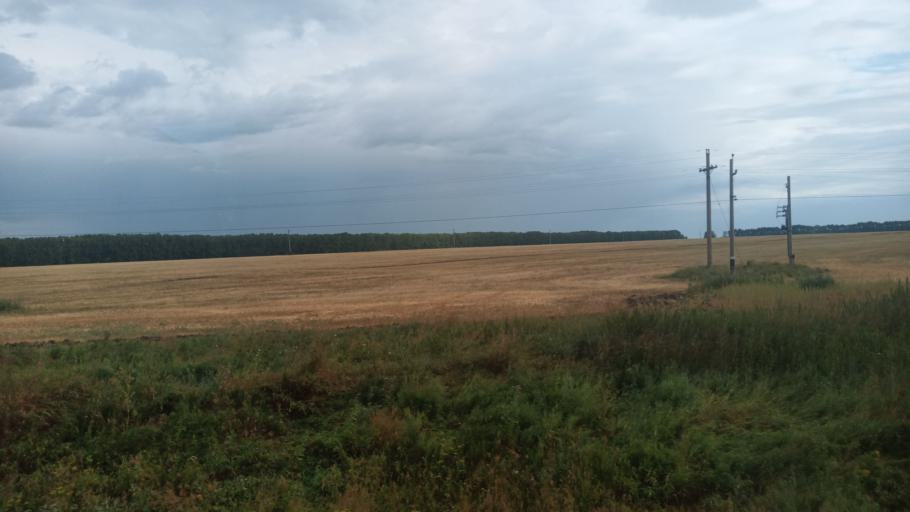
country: RU
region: Altai Krai
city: Nalobikha
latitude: 53.2360
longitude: 84.4647
